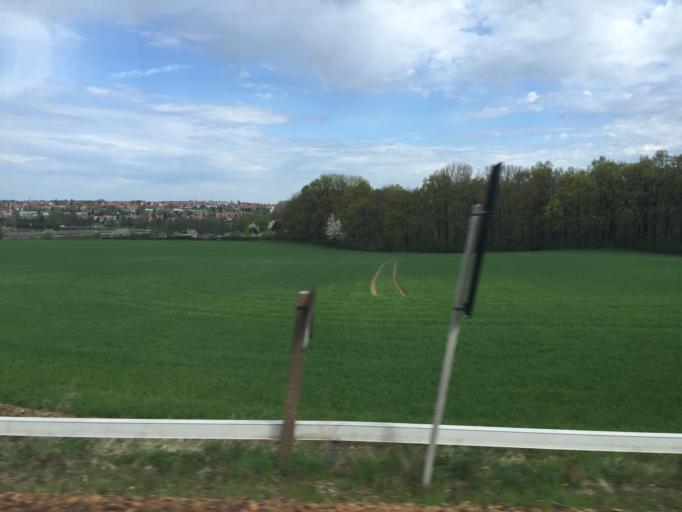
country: DE
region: Saxony
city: Bautzen
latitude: 51.1607
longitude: 14.4543
